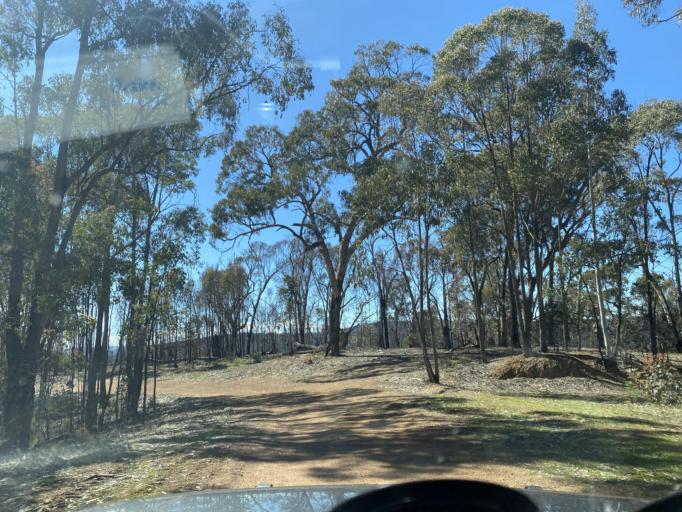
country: AU
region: Victoria
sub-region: Benalla
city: Benalla
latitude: -36.7399
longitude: 146.1791
